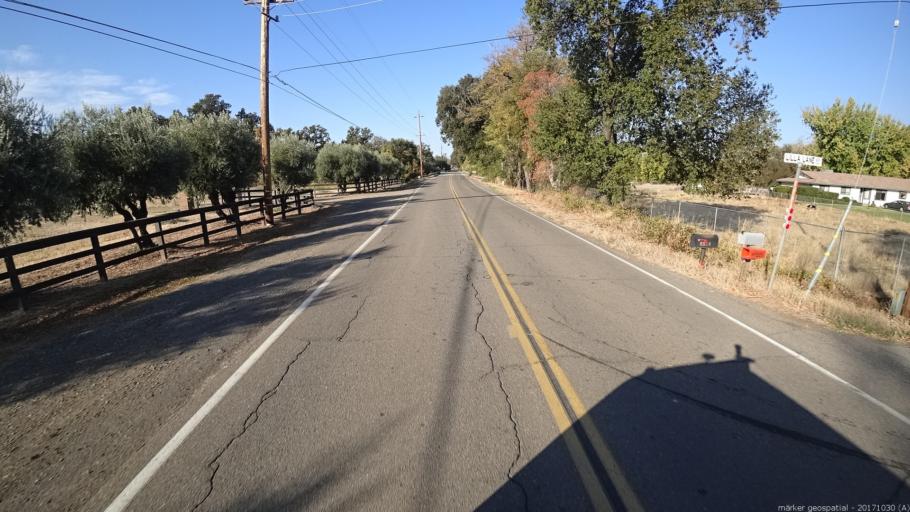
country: US
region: California
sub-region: Shasta County
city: Palo Cedro
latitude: 40.5639
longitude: -122.2254
